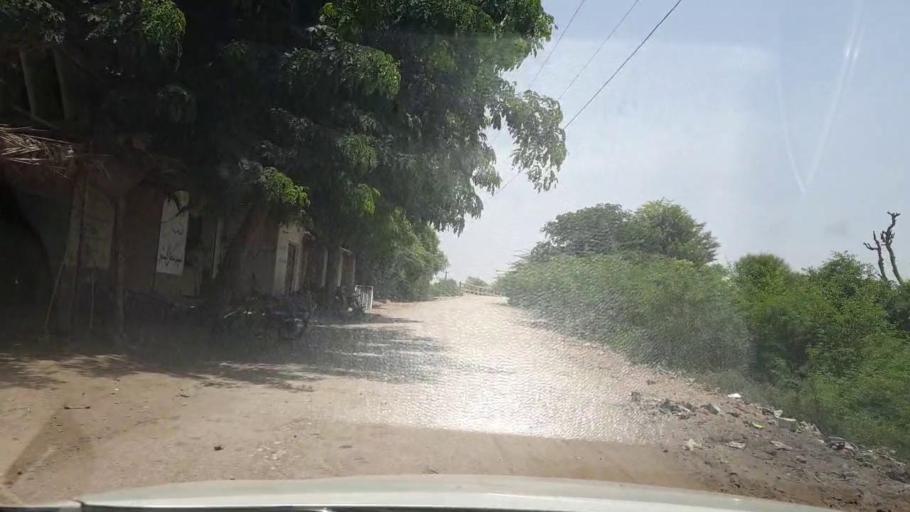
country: PK
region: Sindh
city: Bozdar
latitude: 27.2057
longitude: 68.6669
